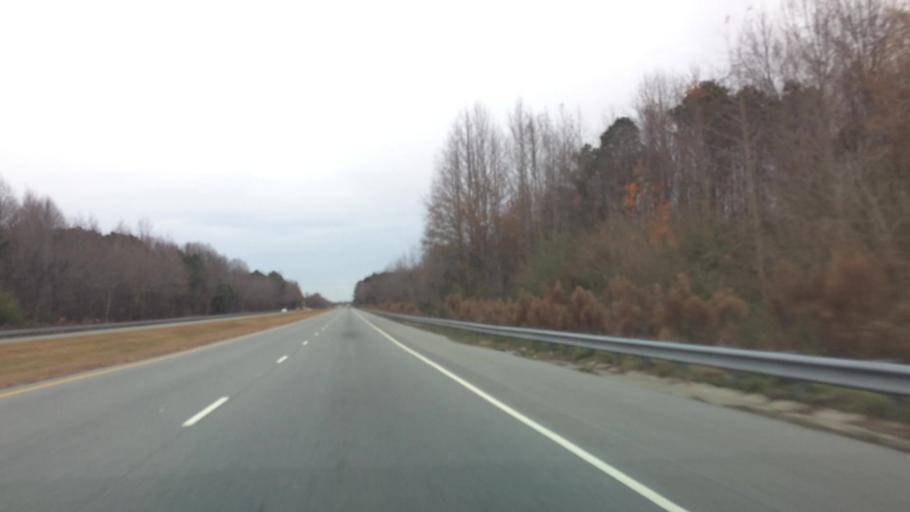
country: US
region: North Carolina
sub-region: Wayne County
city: Mount Olive
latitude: 35.1366
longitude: -78.1380
